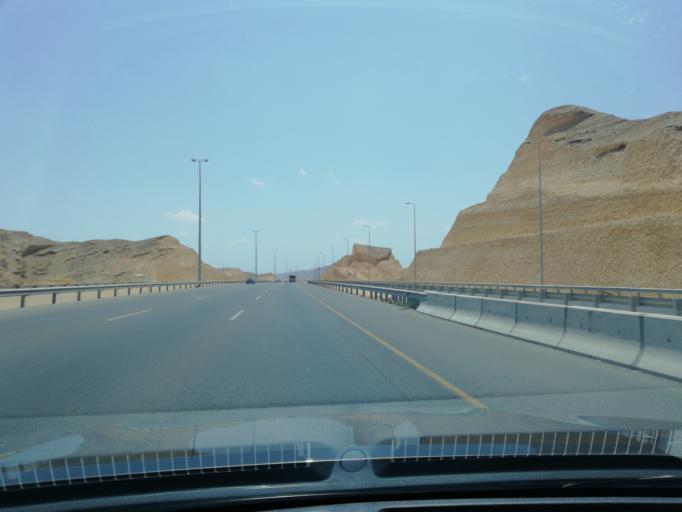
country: OM
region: Muhafazat Masqat
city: As Sib al Jadidah
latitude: 23.5593
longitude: 58.2206
